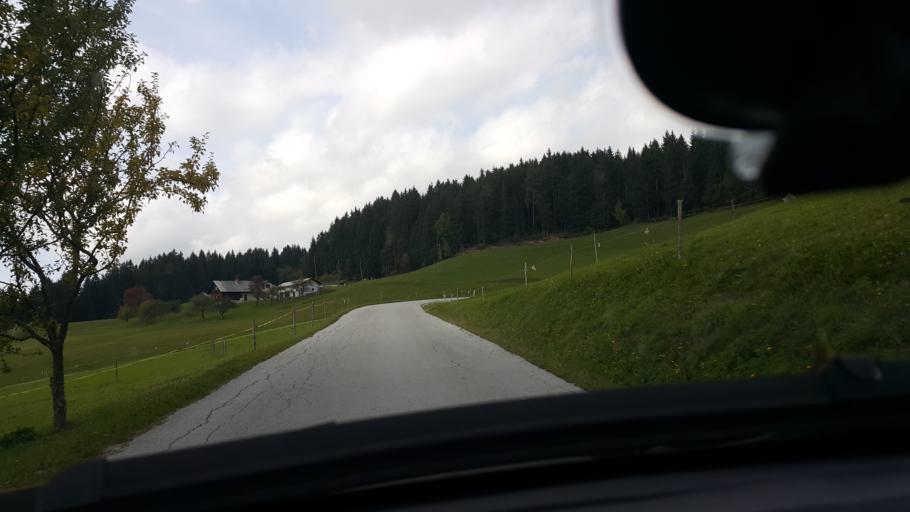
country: SI
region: Vitanje
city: Vitanje
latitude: 46.4085
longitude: 15.2847
